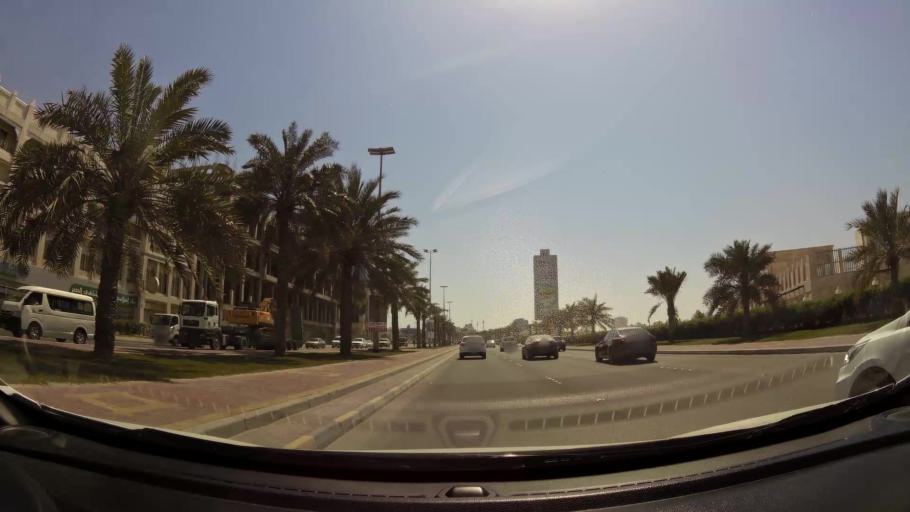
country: BH
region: Manama
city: Manama
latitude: 26.2130
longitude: 50.5969
